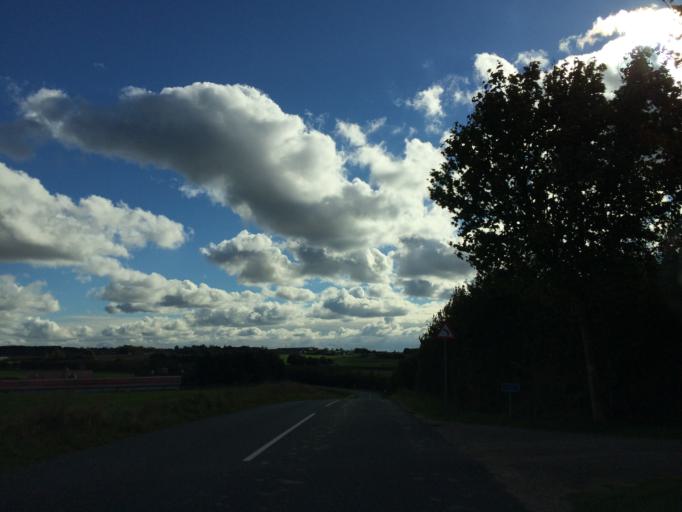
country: DK
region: Central Jutland
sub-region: Skanderborg Kommune
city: Ry
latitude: 56.1913
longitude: 9.7642
